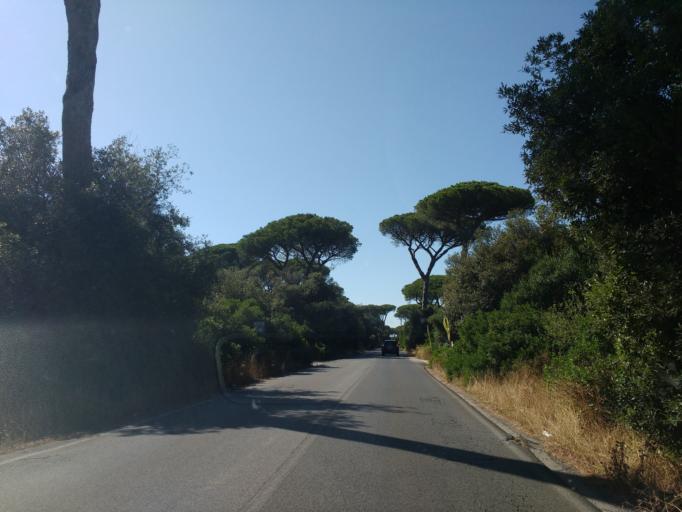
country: IT
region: Latium
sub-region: Citta metropolitana di Roma Capitale
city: Acilia-Castel Fusano-Ostia Antica
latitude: 41.7194
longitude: 12.3494
